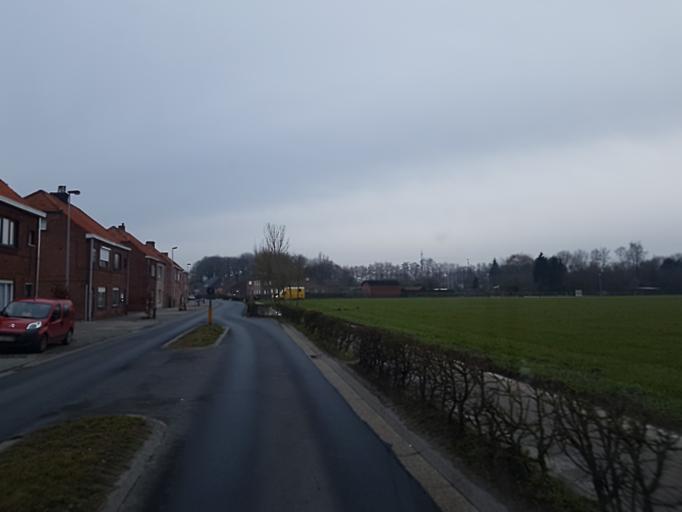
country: BE
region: Flanders
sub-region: Provincie Oost-Vlaanderen
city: Waarschoot
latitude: 51.1682
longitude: 3.6161
